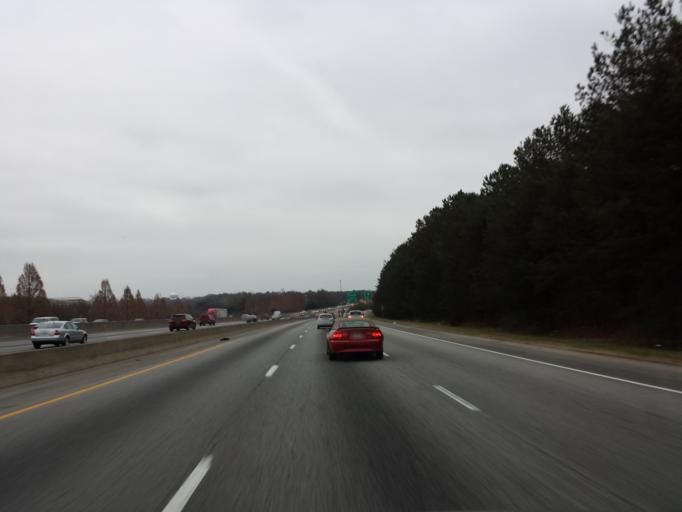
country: US
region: Georgia
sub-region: Fulton County
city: Hapeville
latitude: 33.6317
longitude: -84.4094
